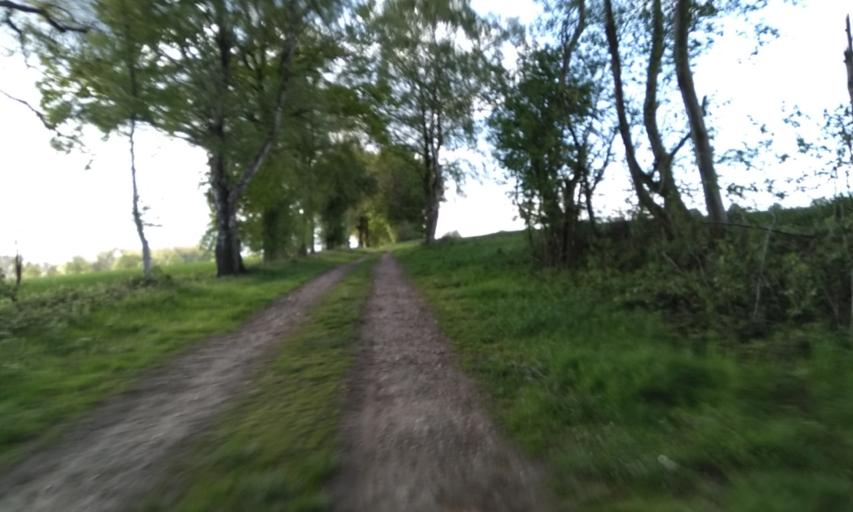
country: DE
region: Lower Saxony
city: Beckdorf
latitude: 53.4092
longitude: 9.6422
